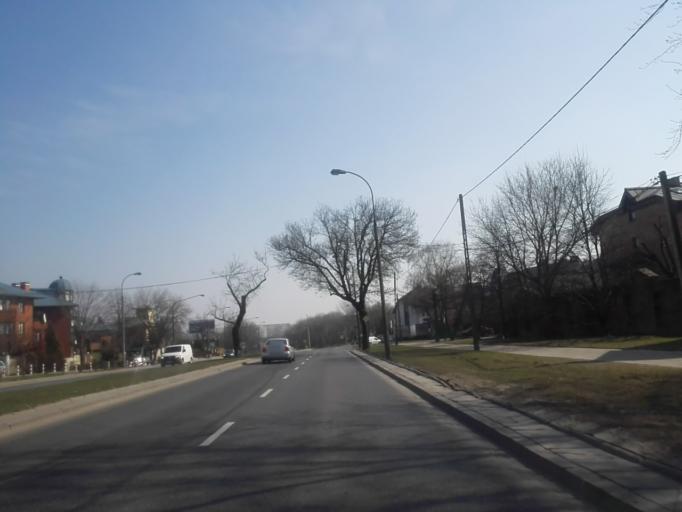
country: PL
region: Masovian Voivodeship
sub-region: Warszawa
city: Mokotow
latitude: 52.1776
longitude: 21.0318
